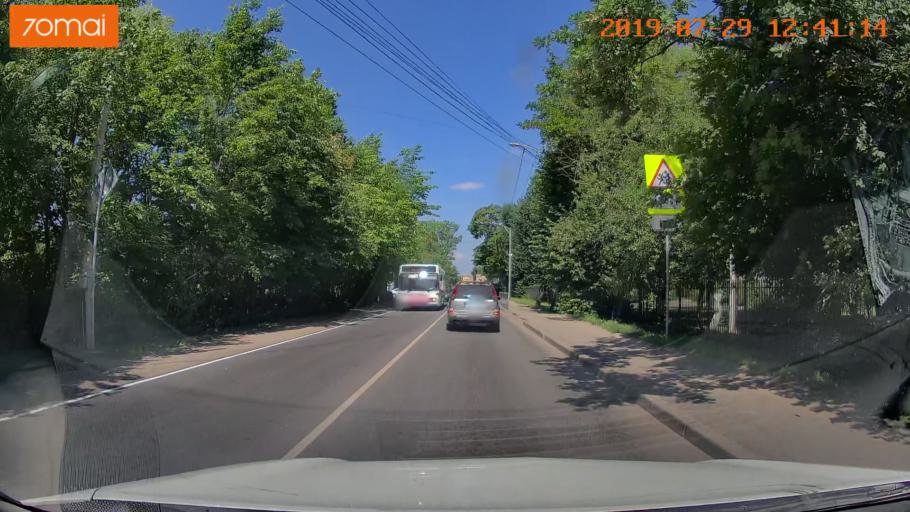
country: RU
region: Kaliningrad
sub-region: Gorod Kaliningrad
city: Kaliningrad
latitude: 54.6715
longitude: 20.5452
